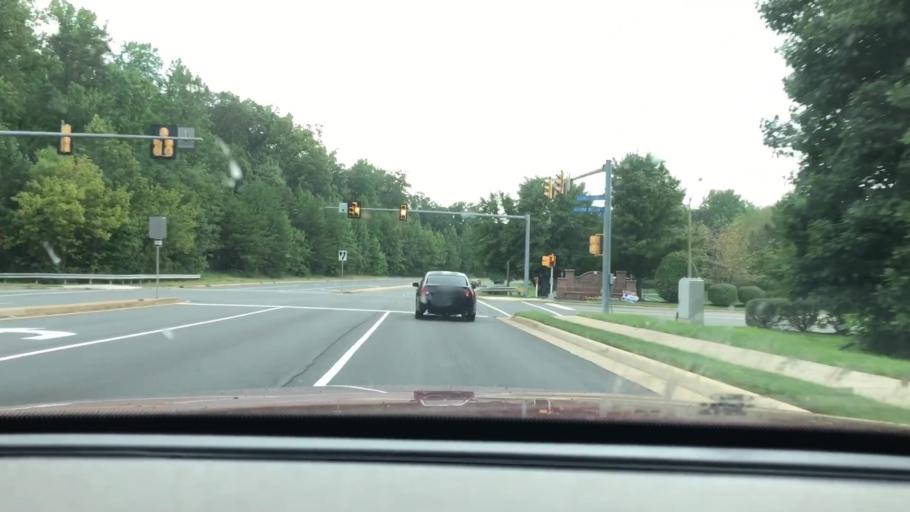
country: US
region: Virginia
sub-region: Fairfax County
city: Centreville
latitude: 38.8447
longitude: -77.4029
